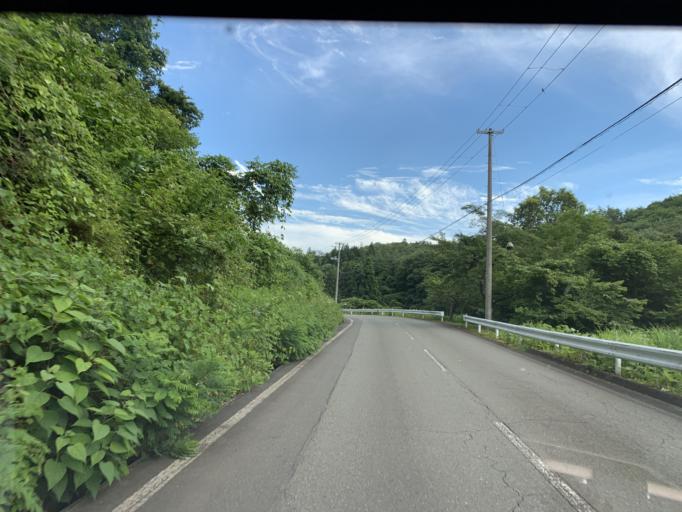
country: JP
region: Iwate
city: Ichinoseki
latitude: 38.8978
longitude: 141.0048
